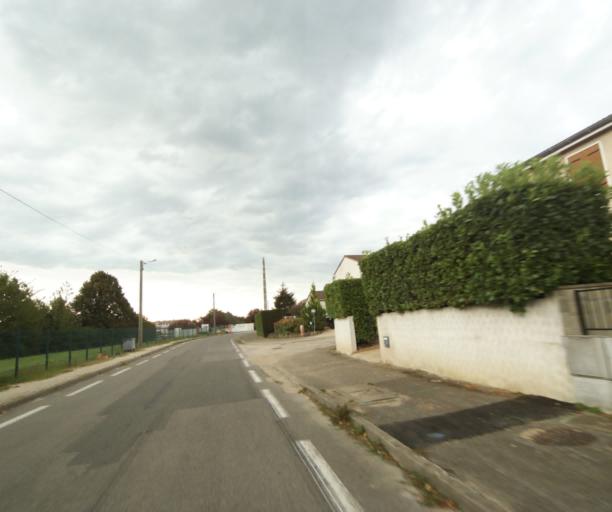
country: FR
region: Bourgogne
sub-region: Departement de Saone-et-Loire
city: Tournus
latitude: 46.5694
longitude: 4.9017
